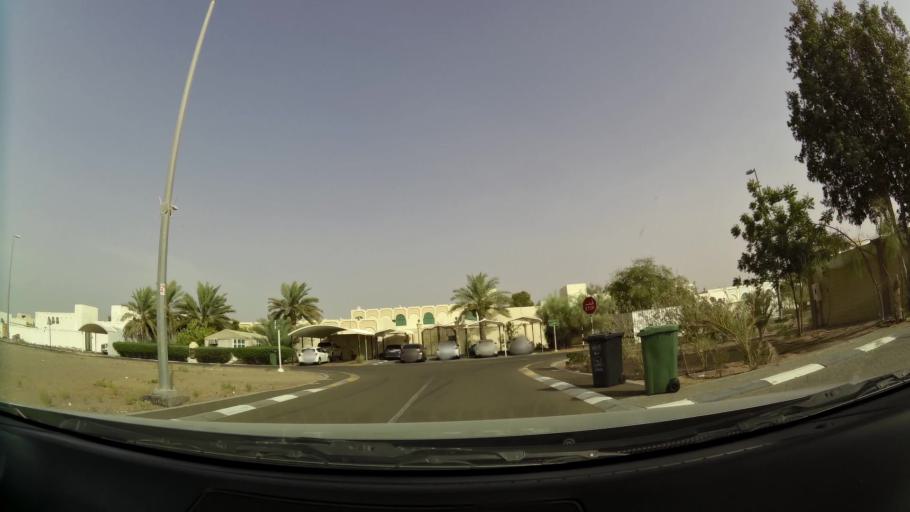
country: AE
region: Abu Dhabi
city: Al Ain
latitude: 24.2064
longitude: 55.5927
